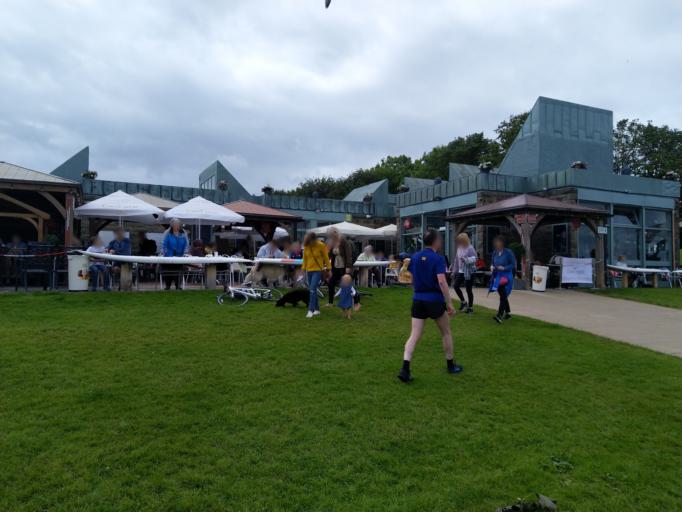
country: GB
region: Scotland
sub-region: Fife
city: Aberdour
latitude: 55.9797
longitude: -3.2793
